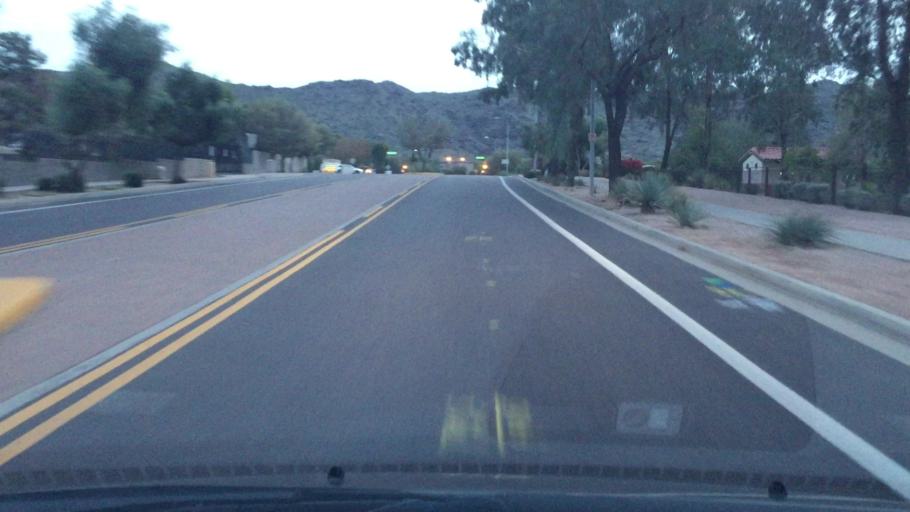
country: US
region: Arizona
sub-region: Maricopa County
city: Guadalupe
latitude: 33.3803
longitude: -112.0128
